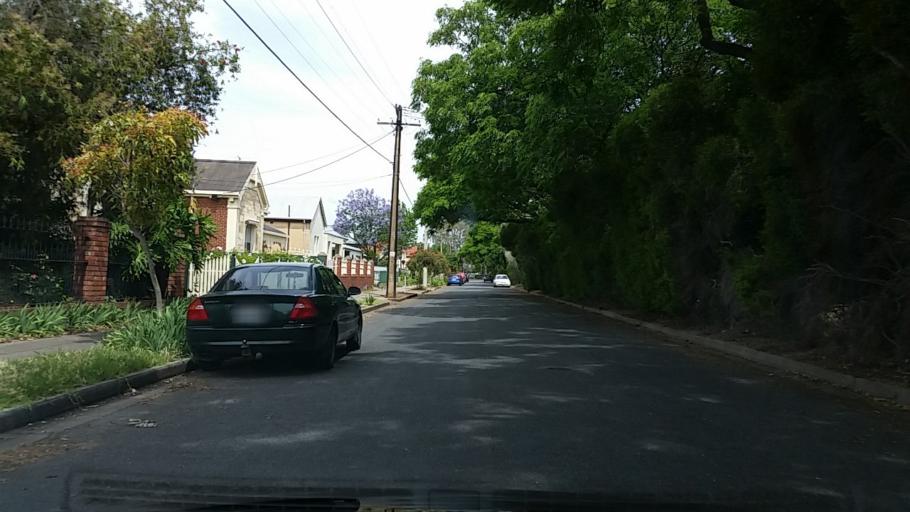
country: AU
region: South Australia
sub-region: Charles Sturt
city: Allenby Gardens
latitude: -34.8954
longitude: 138.5620
